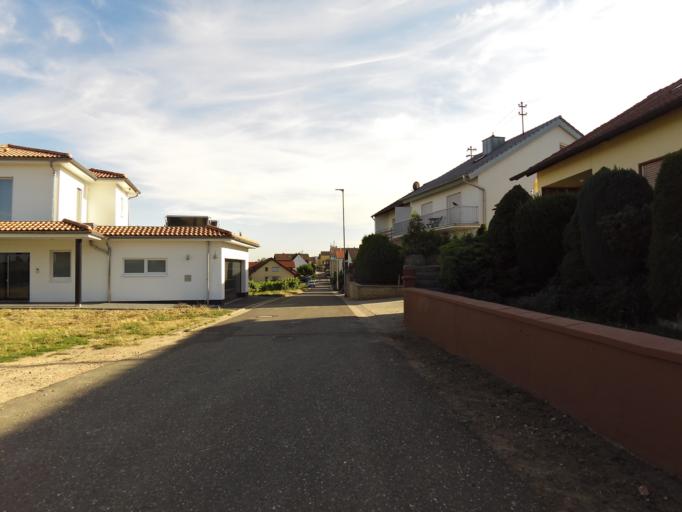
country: DE
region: Rheinland-Pfalz
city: Herxheim am Berg
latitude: 49.5133
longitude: 8.1811
